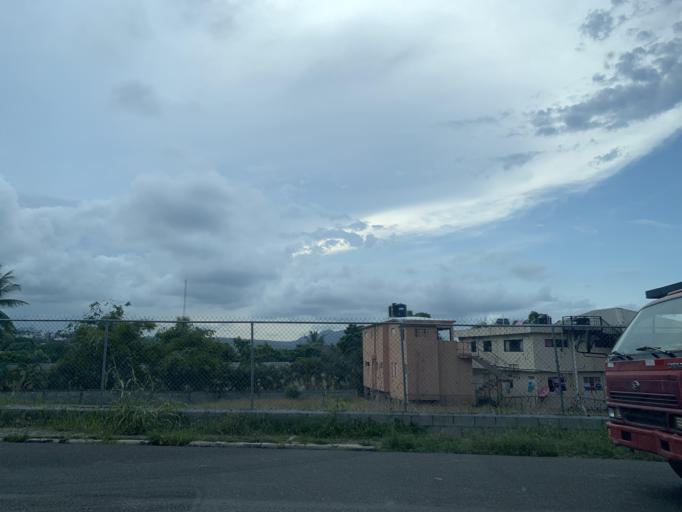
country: DO
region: Puerto Plata
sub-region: Puerto Plata
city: Puerto Plata
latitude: 19.7910
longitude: -70.6935
